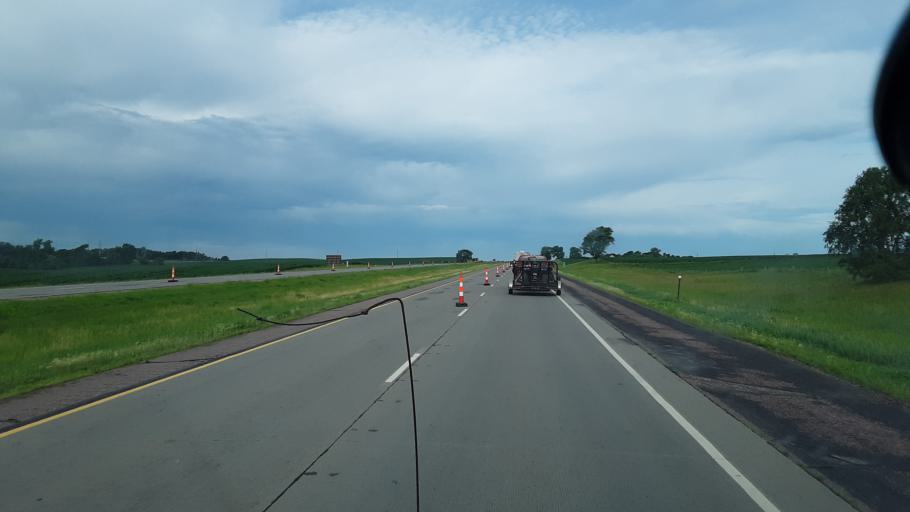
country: US
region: South Dakota
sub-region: Minnehaha County
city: Crooks
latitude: 43.6087
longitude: -96.8575
